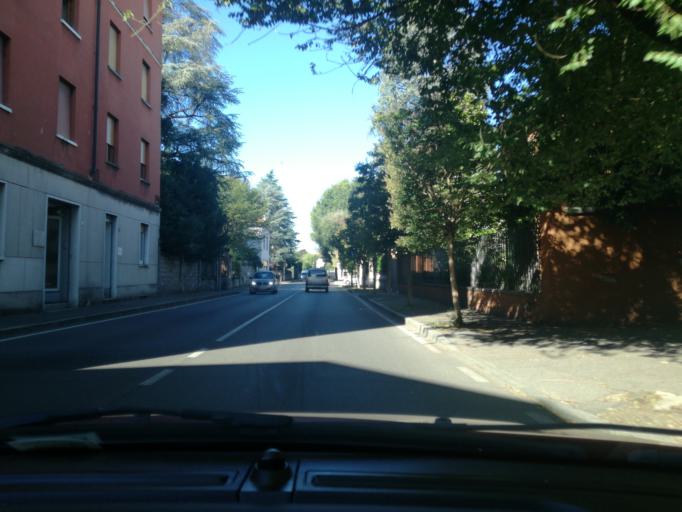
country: IT
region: Lombardy
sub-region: Provincia di Monza e Brianza
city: Seregno
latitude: 45.6562
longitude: 9.2069
